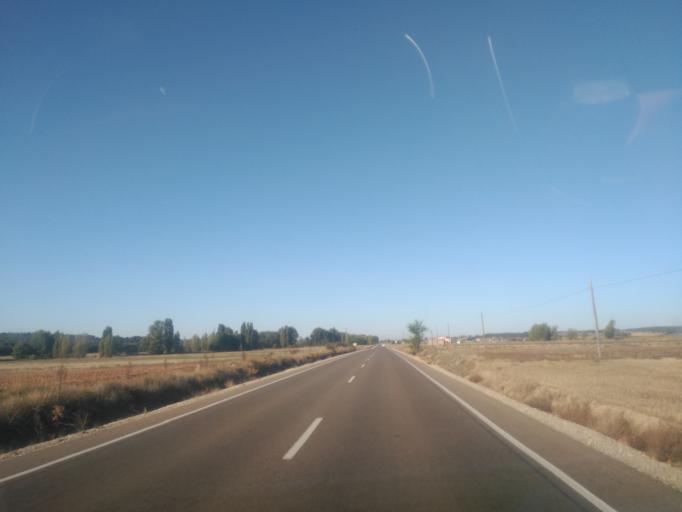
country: ES
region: Castille and Leon
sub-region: Provincia de Burgos
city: Quemada
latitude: 41.6914
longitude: -3.5979
